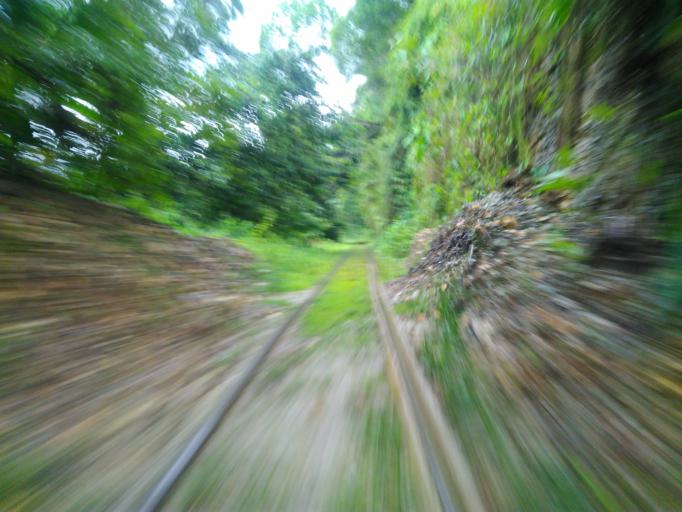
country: CO
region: Valle del Cauca
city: Buenaventura
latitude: 3.8438
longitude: -76.8768
